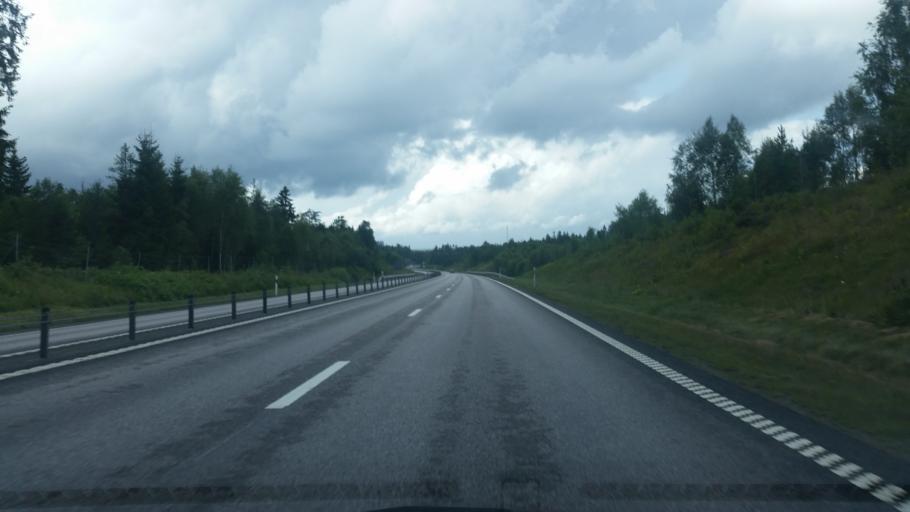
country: SE
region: Vaestra Goetaland
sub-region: Boras Kommun
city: Ganghester
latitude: 57.6532
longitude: 13.0557
